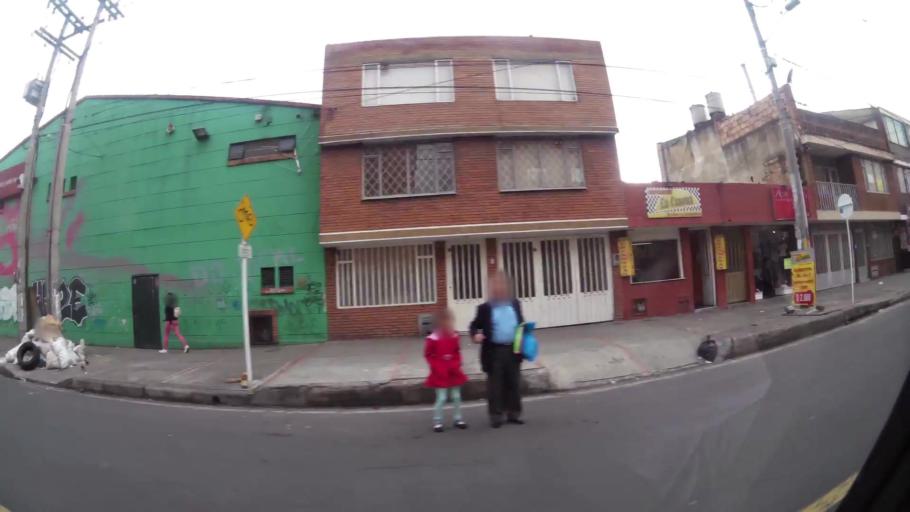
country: CO
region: Bogota D.C.
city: Barrio San Luis
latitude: 4.7195
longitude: -74.0712
